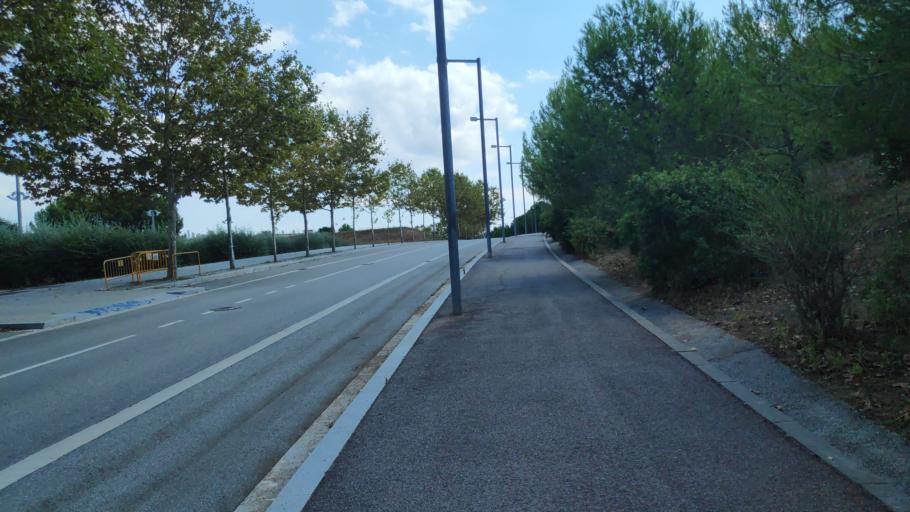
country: ES
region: Catalonia
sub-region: Provincia de Barcelona
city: Sant Cugat del Valles
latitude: 41.4770
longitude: 2.0633
